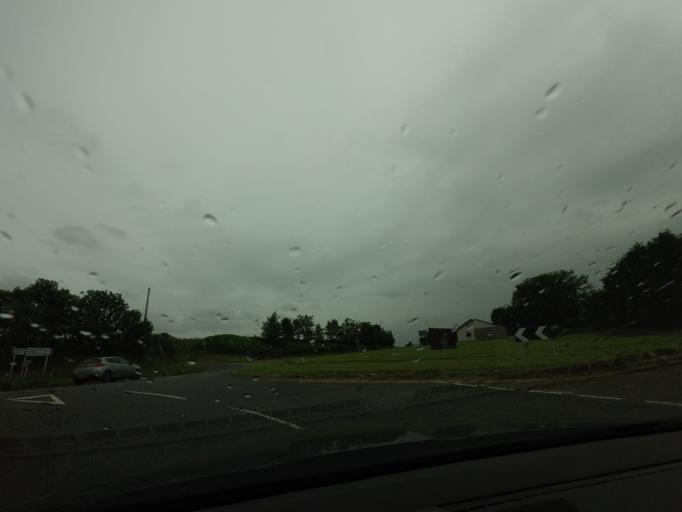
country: GB
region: Scotland
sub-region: Aberdeenshire
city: Aberchirder
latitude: 57.5936
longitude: -2.6207
